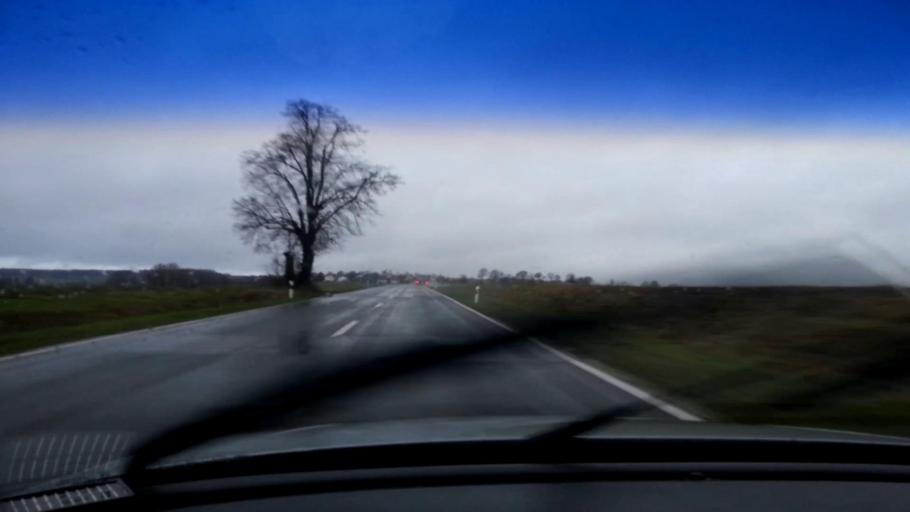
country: DE
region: Bavaria
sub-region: Upper Franconia
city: Schesslitz
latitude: 49.9918
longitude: 11.0073
